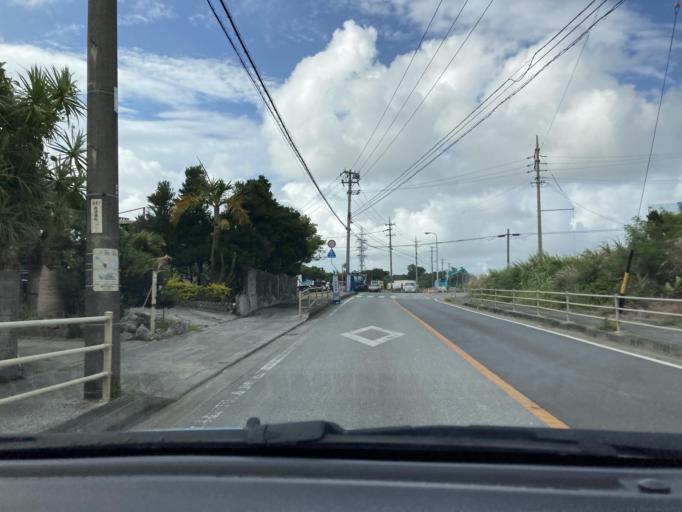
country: JP
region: Okinawa
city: Itoman
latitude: 26.1052
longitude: 127.6953
